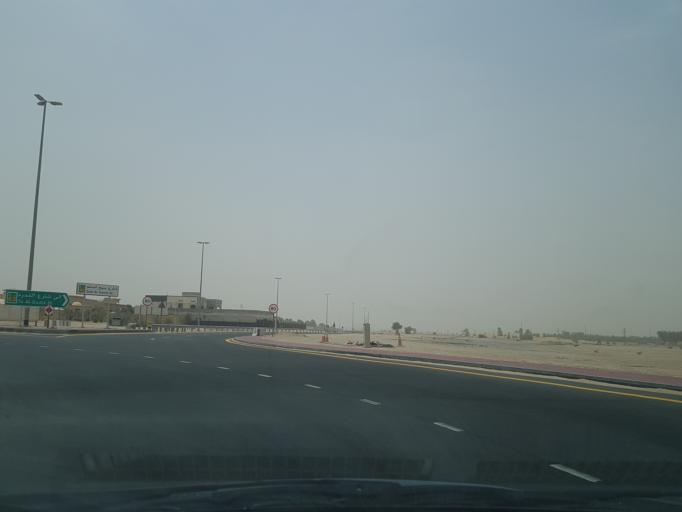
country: AE
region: Dubai
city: Dubai
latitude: 24.9308
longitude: 55.4684
